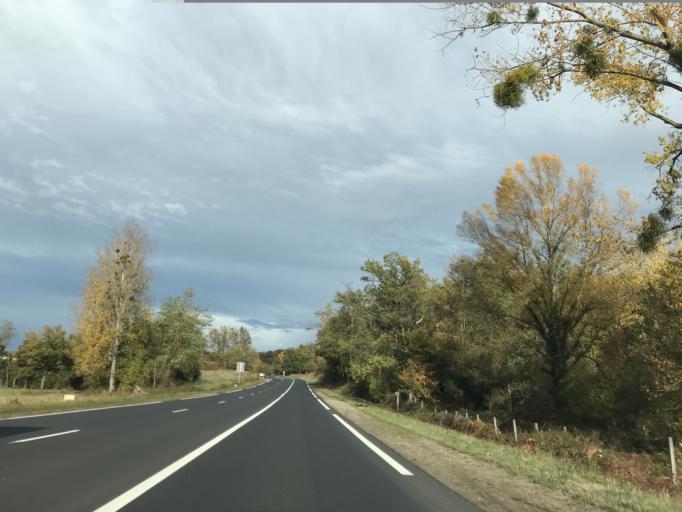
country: FR
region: Auvergne
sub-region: Departement du Puy-de-Dome
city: Peschadoires
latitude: 45.8496
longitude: 3.5073
